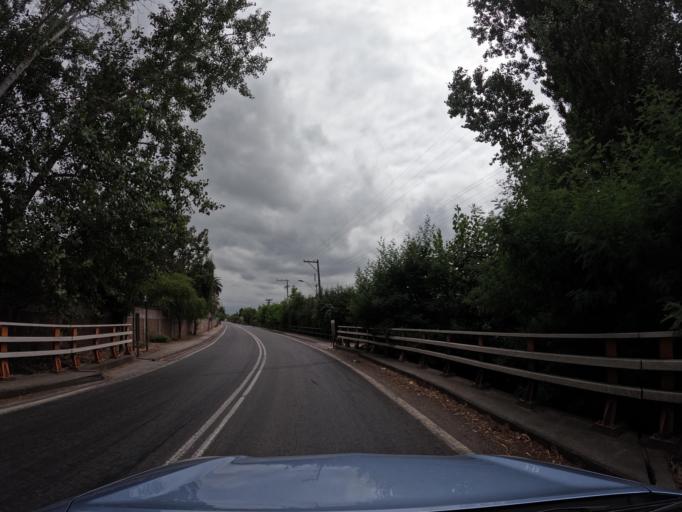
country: CL
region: Maule
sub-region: Provincia de Curico
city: Teno
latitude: -34.7550
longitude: -71.2389
